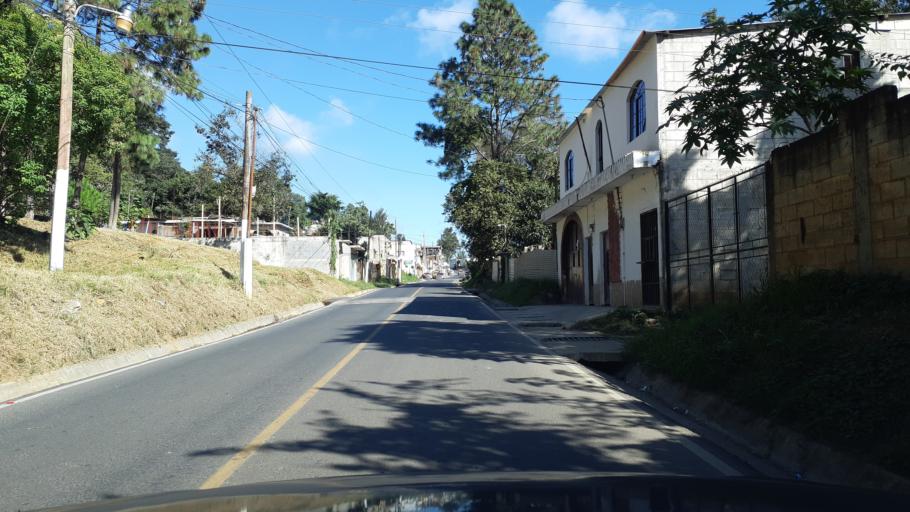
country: GT
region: Chimaltenango
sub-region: Municipio de Chimaltenango
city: Chimaltenango
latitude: 14.6501
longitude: -90.8203
